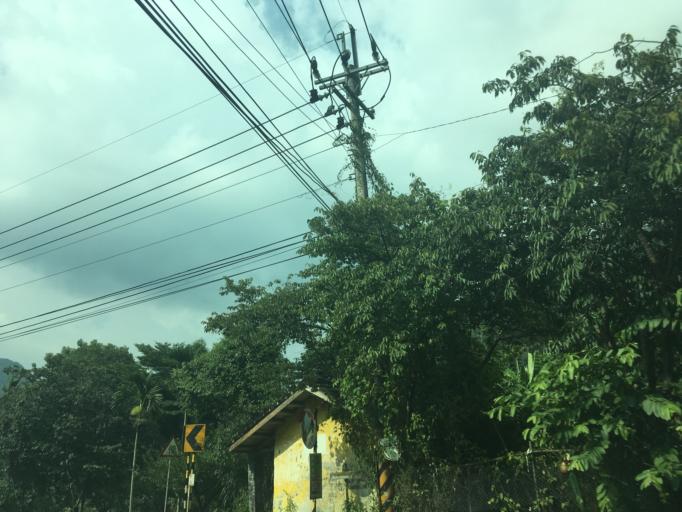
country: TW
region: Taiwan
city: Fengyuan
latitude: 24.3354
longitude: 120.9347
